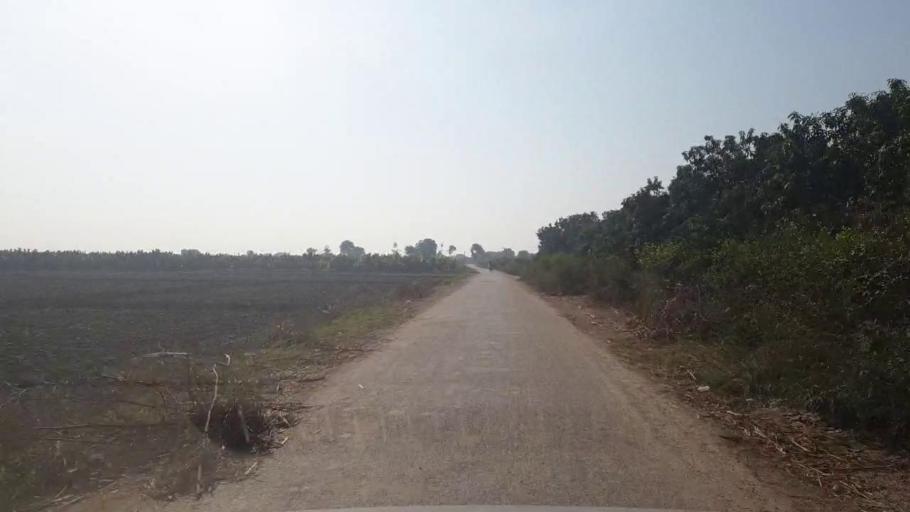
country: PK
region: Sindh
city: Tando Allahyar
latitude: 25.4710
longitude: 68.7433
